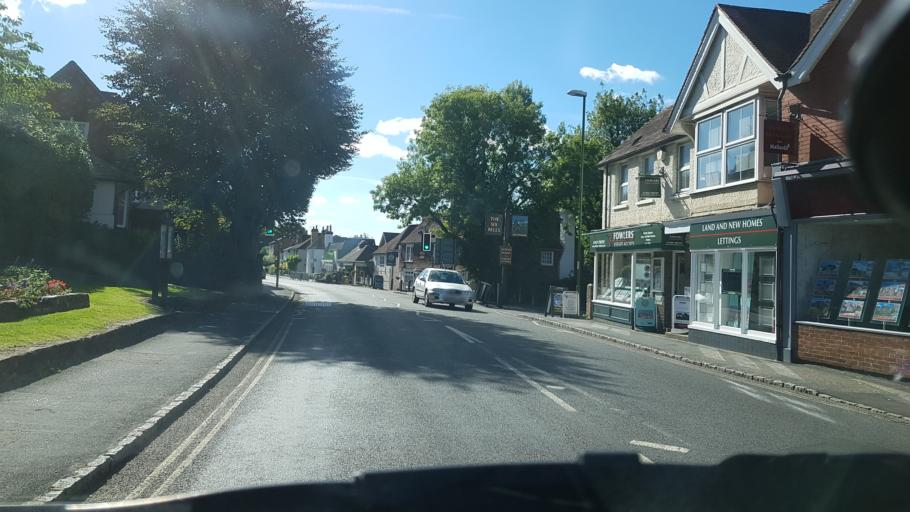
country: GB
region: England
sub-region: West Sussex
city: Billingshurst
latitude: 51.0230
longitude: -0.4517
